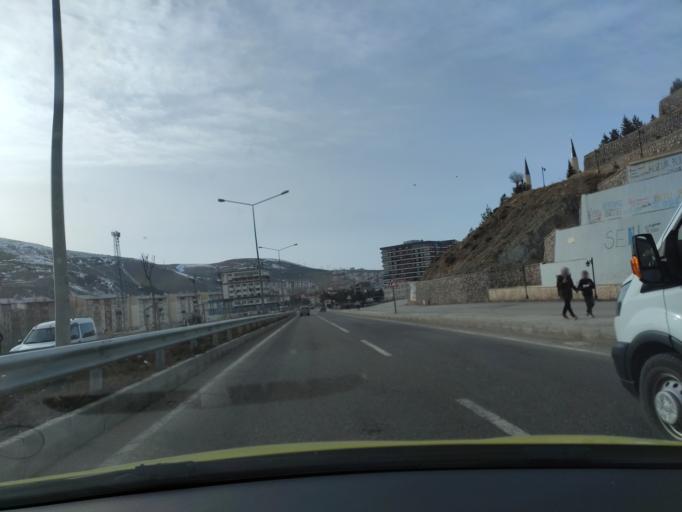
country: TR
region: Bayburt
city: Bayburt
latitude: 40.2441
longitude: 40.2386
